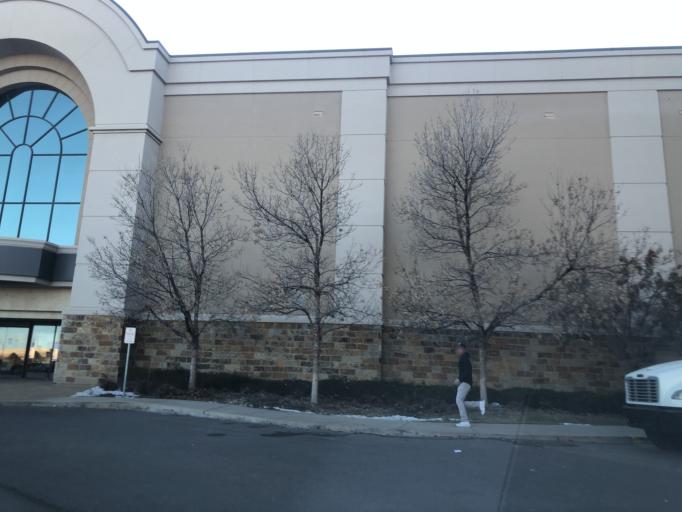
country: US
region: Colorado
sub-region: Adams County
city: Aurora
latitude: 39.7080
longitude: -104.8225
